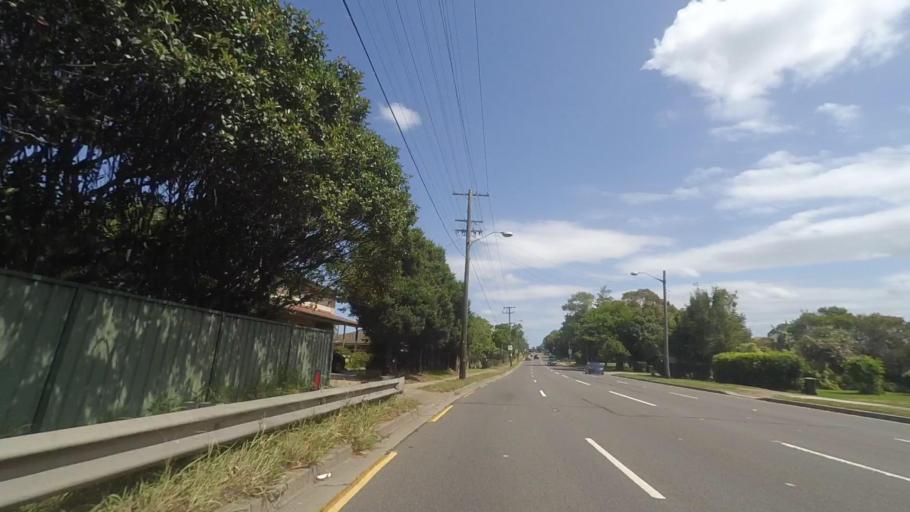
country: AU
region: New South Wales
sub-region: Parramatta
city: Carlingford
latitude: -33.7707
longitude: 151.0511
